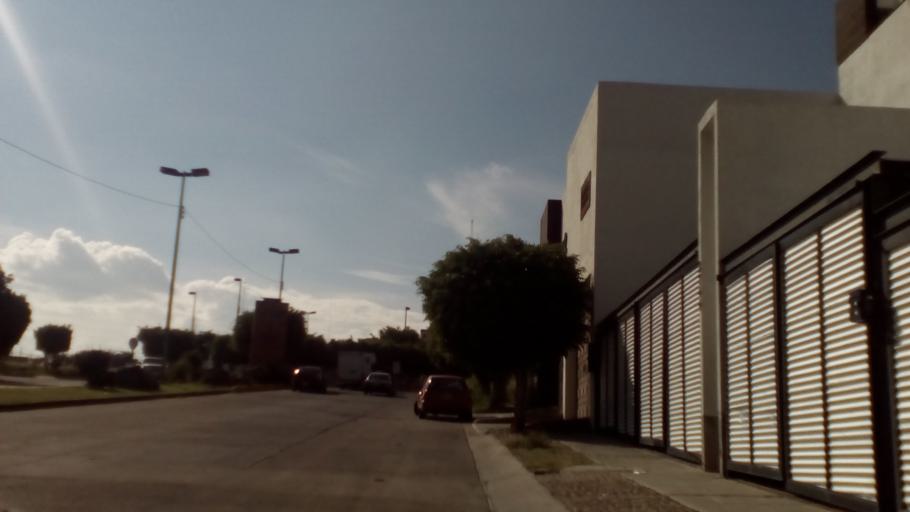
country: MX
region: Guanajuato
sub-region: Leon
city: La Ermita
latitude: 21.1527
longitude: -101.7259
